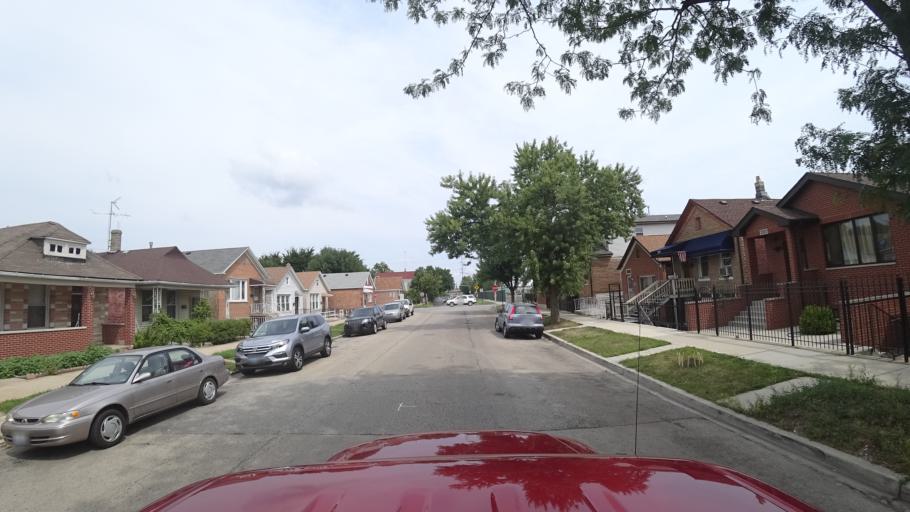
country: US
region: Illinois
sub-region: Cook County
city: Chicago
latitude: 41.8334
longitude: -87.6778
